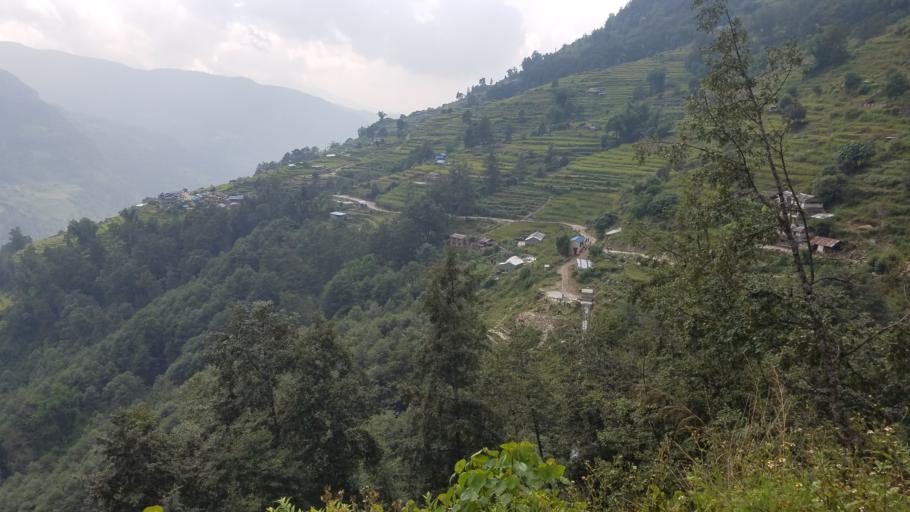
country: NP
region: Western Region
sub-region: Dhawalagiri Zone
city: Chitre
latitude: 28.3648
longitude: 83.8050
